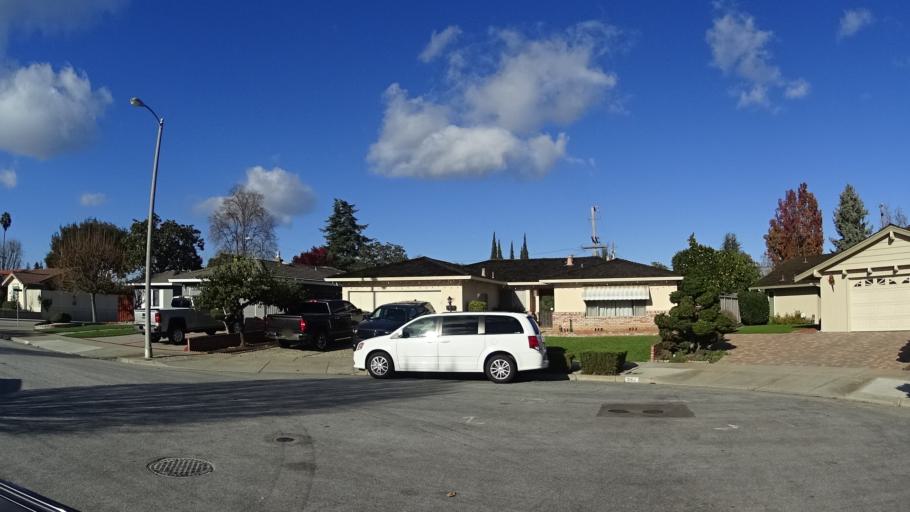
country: US
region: California
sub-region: Santa Clara County
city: Sunnyvale
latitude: 37.3775
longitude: -122.0440
